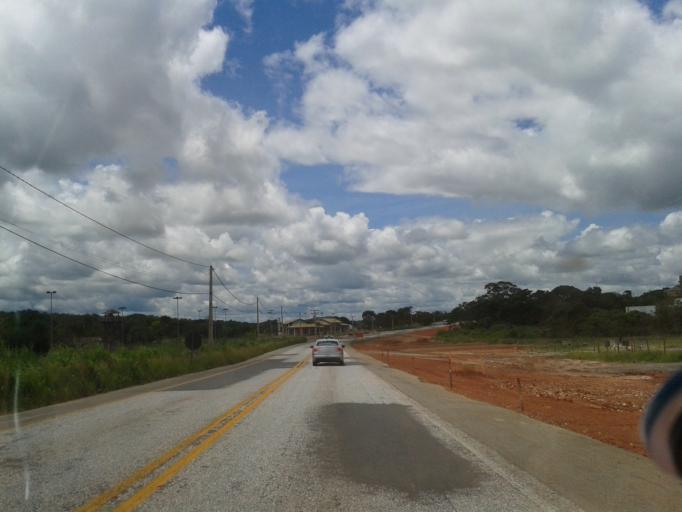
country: BR
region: Goias
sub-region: Goias
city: Goias
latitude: -15.9644
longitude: -50.1260
